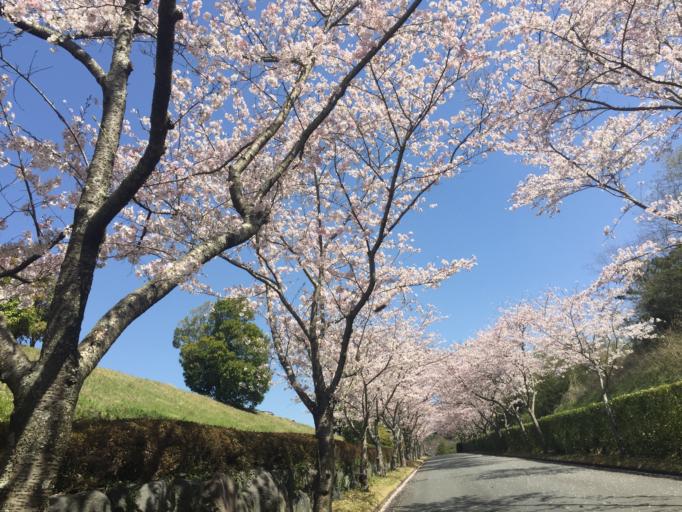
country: JP
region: Shizuoka
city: Kanaya
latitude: 34.7899
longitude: 138.1185
